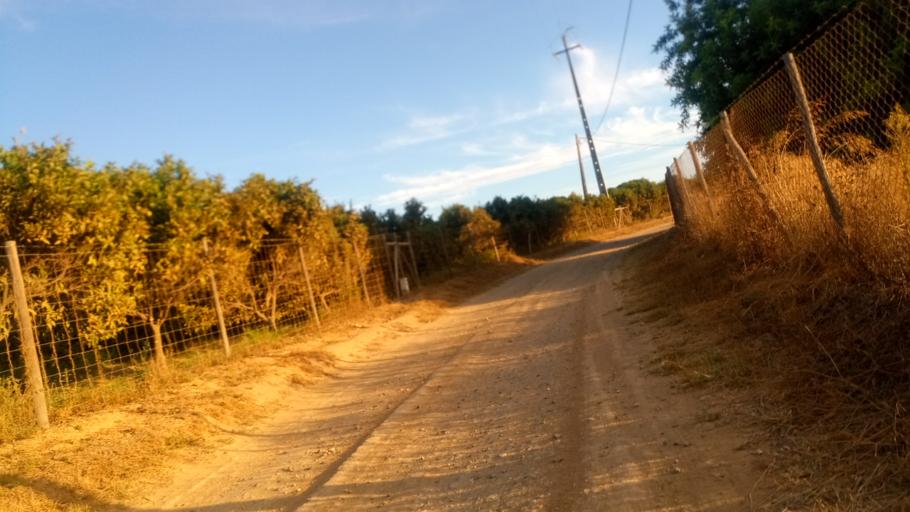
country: PT
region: Faro
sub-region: Tavira
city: Tavira
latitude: 37.1507
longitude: -7.5870
